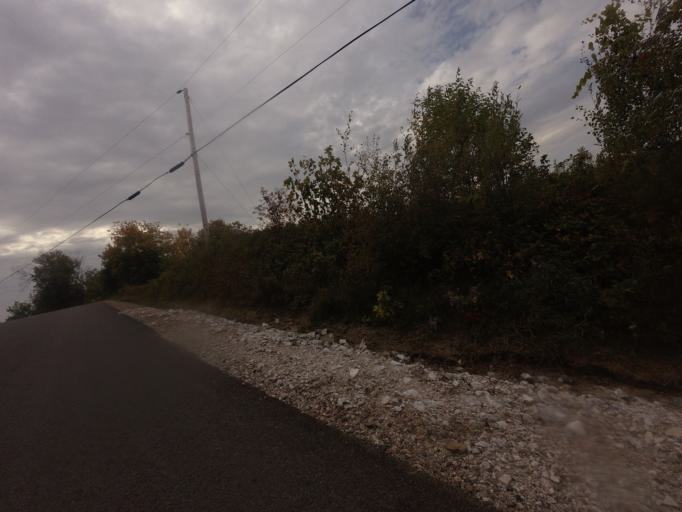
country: CA
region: Quebec
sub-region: Outaouais
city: Wakefield
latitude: 45.9900
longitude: -75.9511
